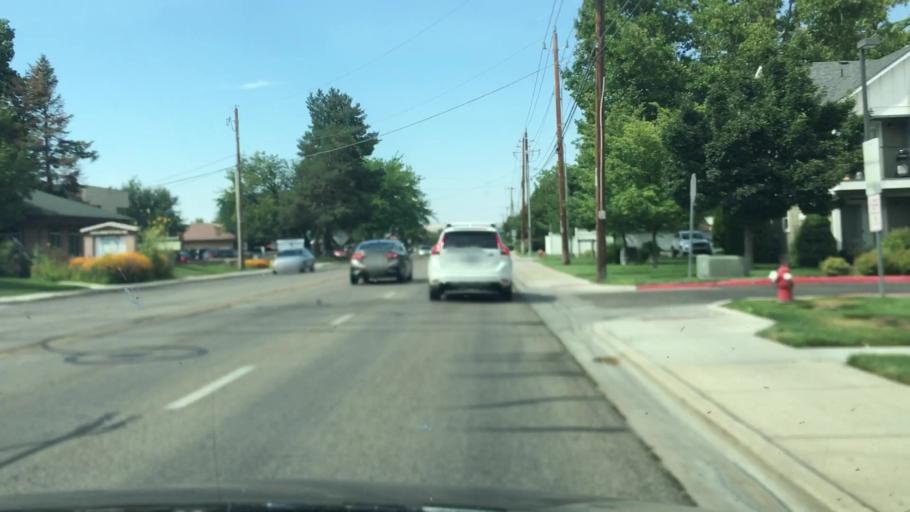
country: US
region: Idaho
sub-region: Ada County
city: Garden City
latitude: 43.6312
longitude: -116.2742
